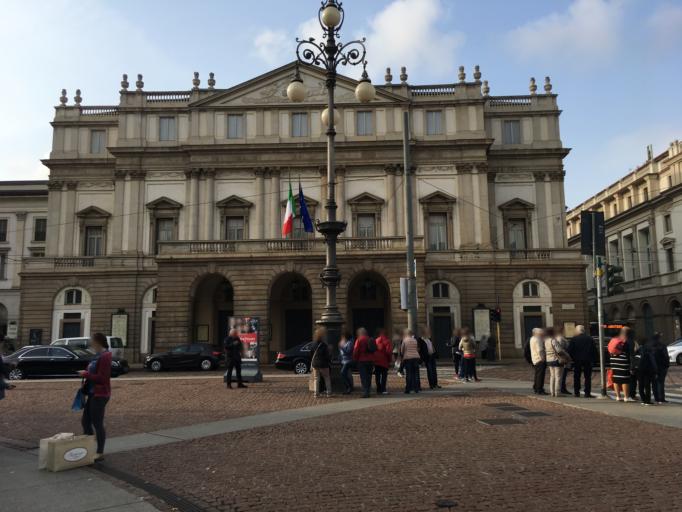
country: IT
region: Lombardy
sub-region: Citta metropolitana di Milano
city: Milano
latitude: 45.4671
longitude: 9.1900
